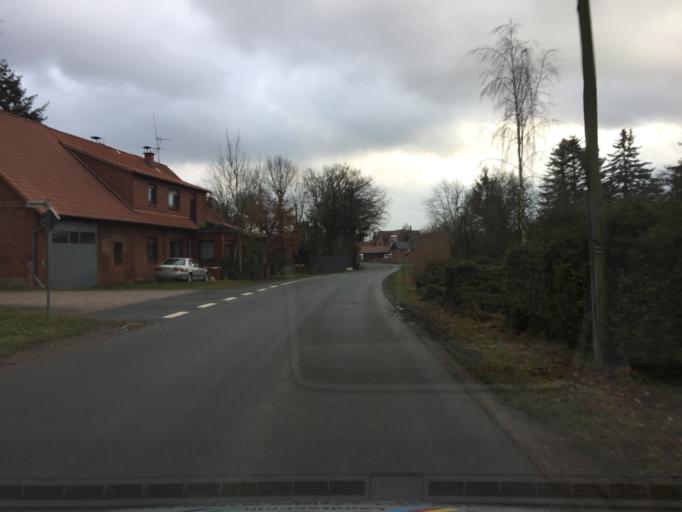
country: DE
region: Lower Saxony
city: Stolzenau
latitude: 52.5241
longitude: 9.0529
